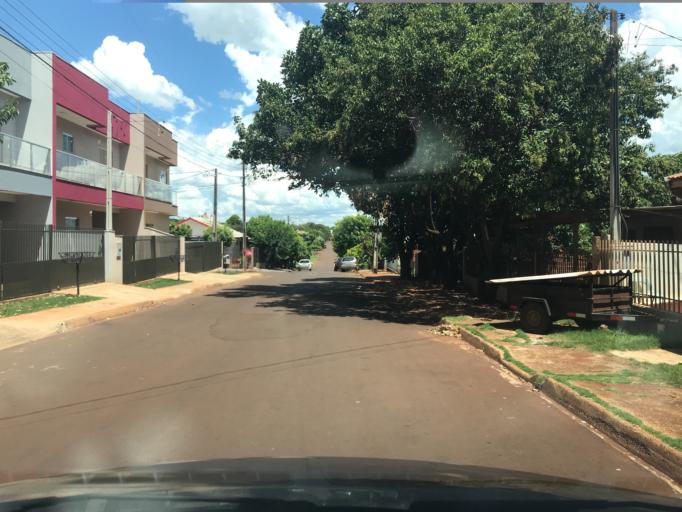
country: BR
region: Parana
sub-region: Palotina
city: Palotina
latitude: -24.2746
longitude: -53.8463
